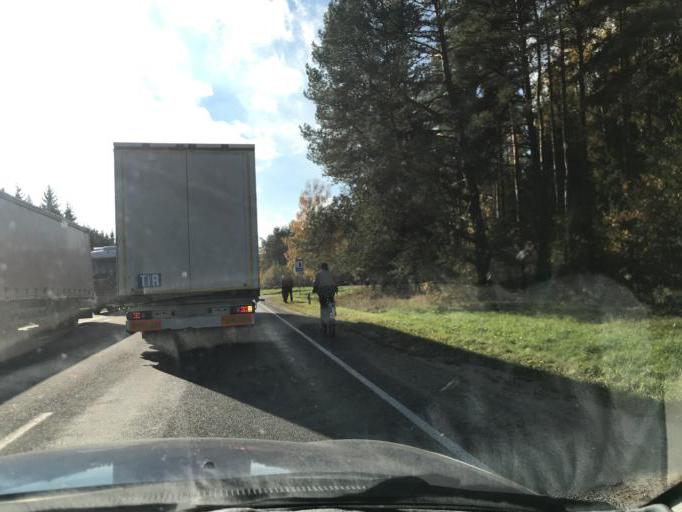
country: LT
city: Salcininkai
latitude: 54.2254
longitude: 25.3569
